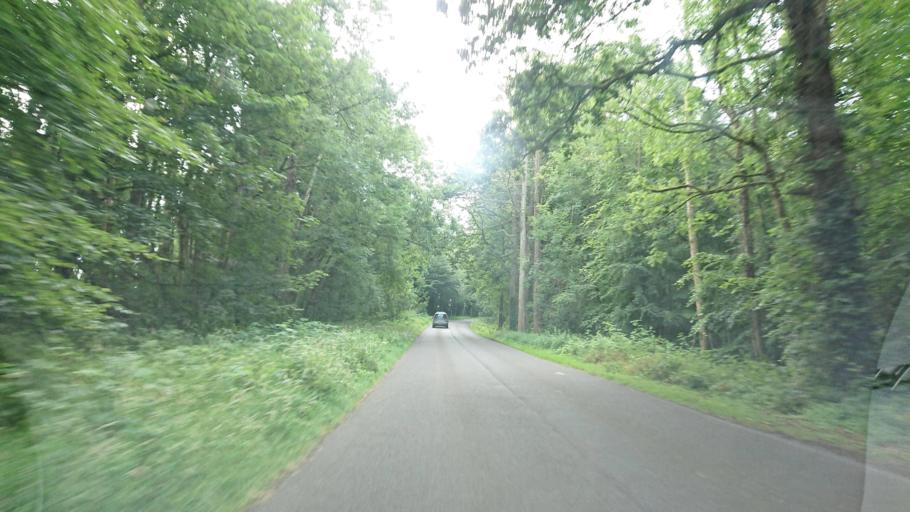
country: IE
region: Connaught
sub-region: Roscommon
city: Boyle
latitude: 53.9730
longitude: -8.2460
